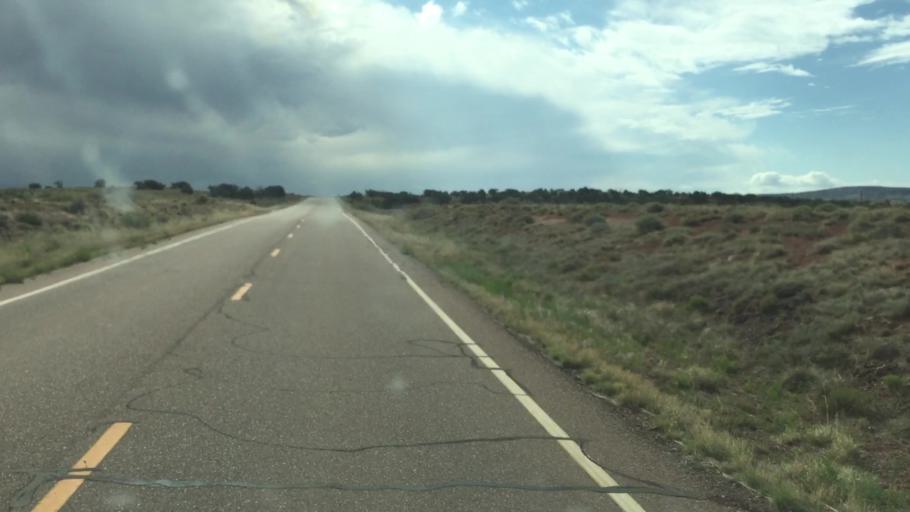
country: US
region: Arizona
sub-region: Apache County
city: Saint Johns
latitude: 34.5135
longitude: -109.6949
